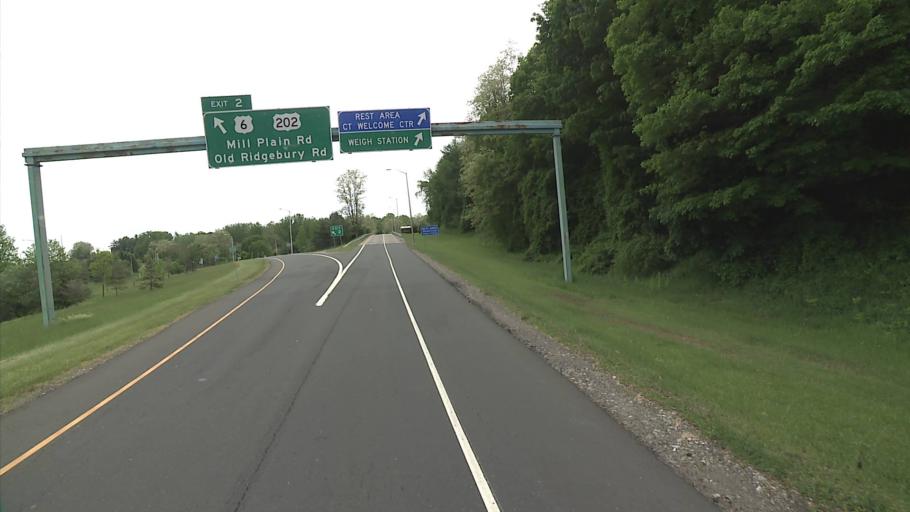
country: US
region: New York
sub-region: Putnam County
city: Peach Lake
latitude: 41.3915
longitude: -73.5254
